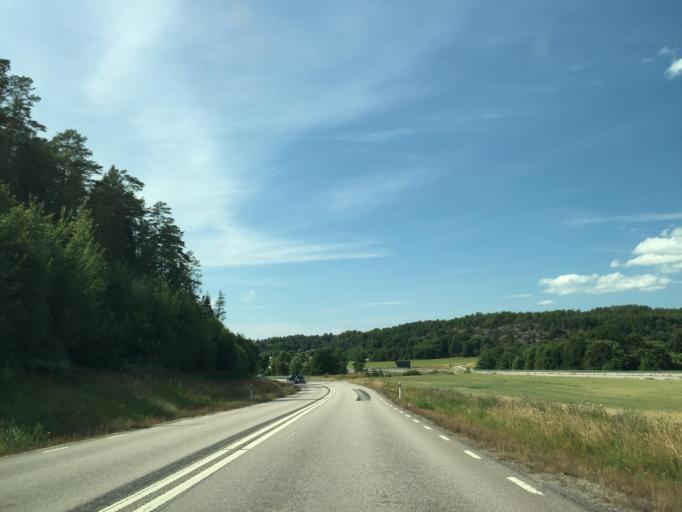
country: SE
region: Vaestra Goetaland
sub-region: Tanums Kommun
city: Tanumshede
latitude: 58.7326
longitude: 11.3227
